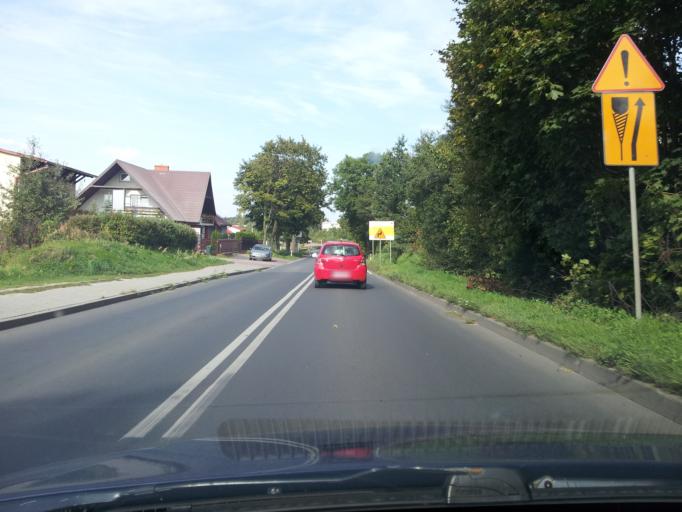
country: PL
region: Kujawsko-Pomorskie
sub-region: Powiat rypinski
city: Rypin
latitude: 53.0739
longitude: 19.4128
